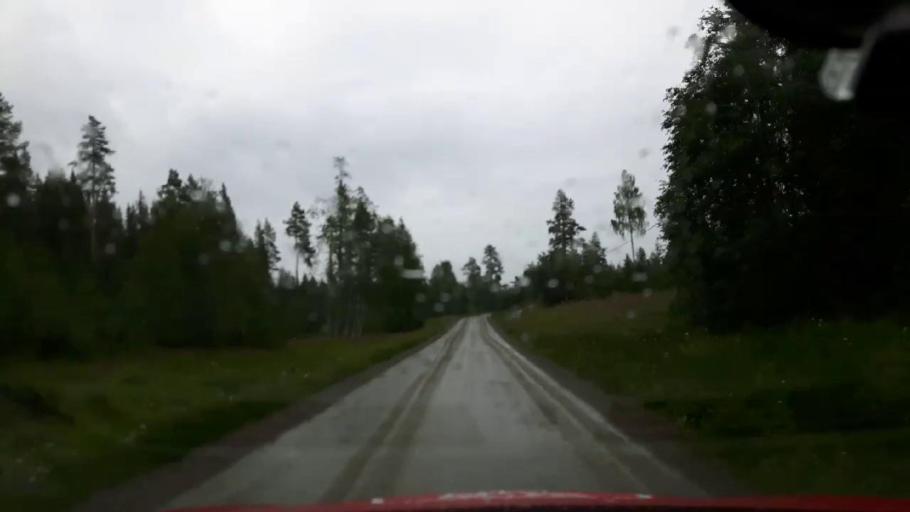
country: SE
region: Jaemtland
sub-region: OEstersunds Kommun
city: Brunflo
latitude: 62.8824
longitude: 14.8775
